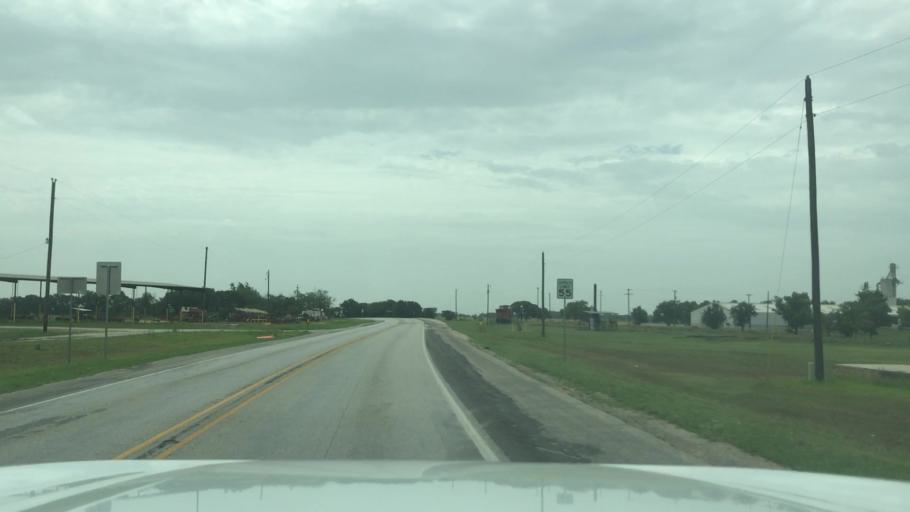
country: US
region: Texas
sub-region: Eastland County
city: Gorman
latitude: 32.2071
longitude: -98.6625
